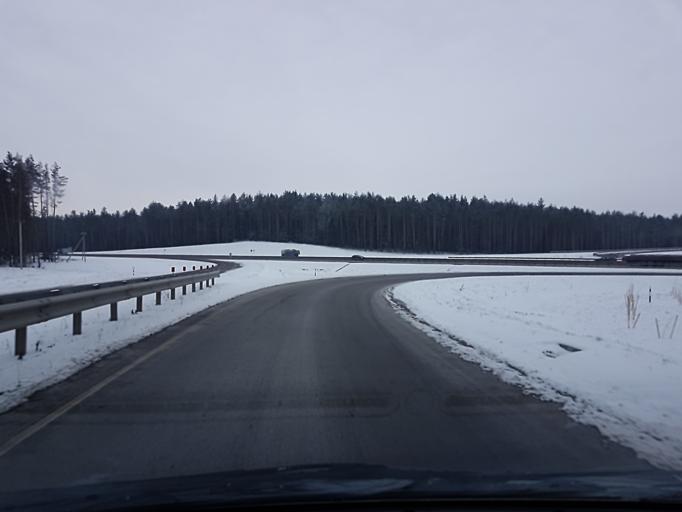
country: BY
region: Minsk
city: Rakaw
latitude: 53.9655
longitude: 27.0913
